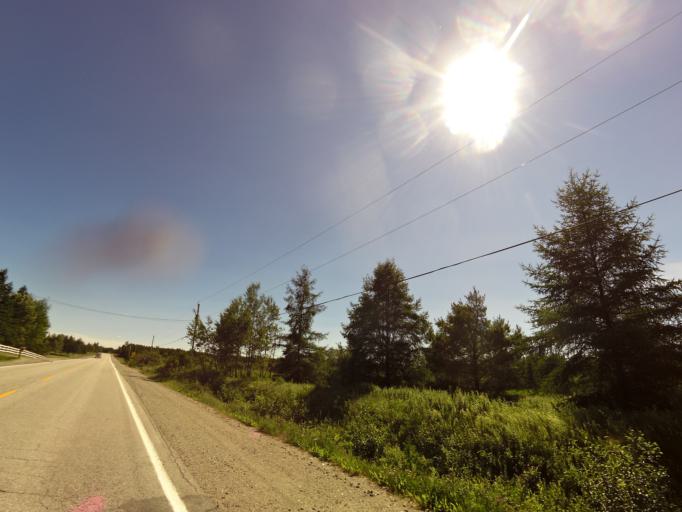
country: CA
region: Quebec
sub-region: Abitibi-Temiscamingue
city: Senneterre
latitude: 48.2874
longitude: -77.3116
